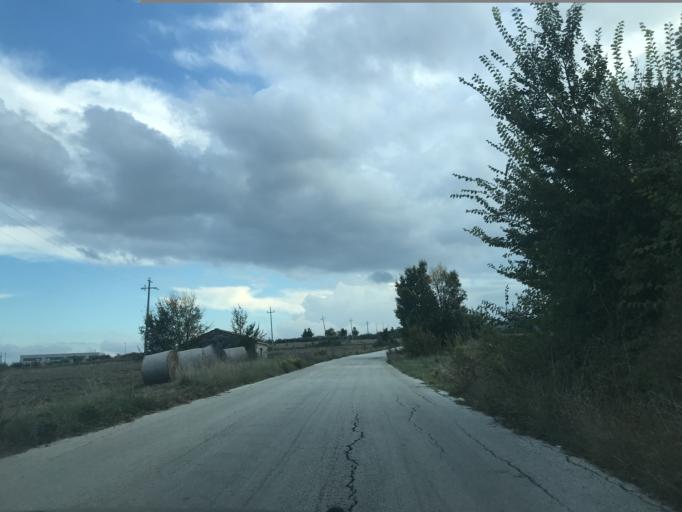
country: IT
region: Molise
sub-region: Provincia di Isernia
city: Bagnoli del Trigno
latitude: 41.6936
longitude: 14.4620
